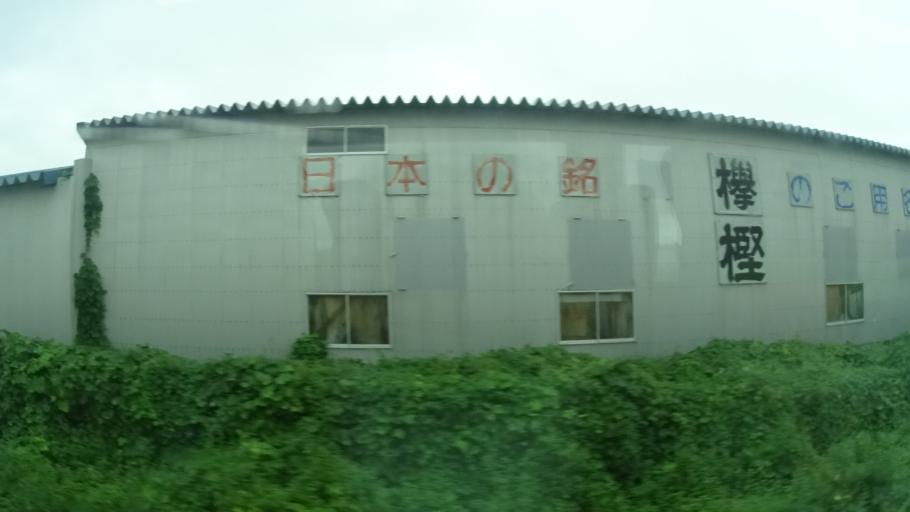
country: JP
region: Yamagata
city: Tsuruoka
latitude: 38.7660
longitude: 139.8912
